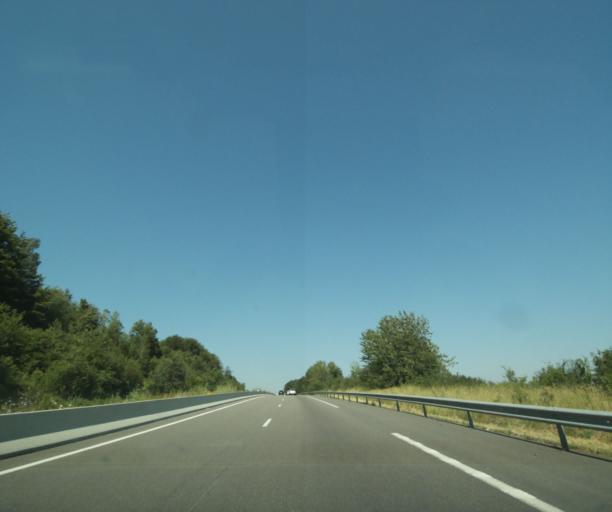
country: FR
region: Lorraine
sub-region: Departement de la Meuse
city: Lerouville
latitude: 48.7062
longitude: 5.4952
